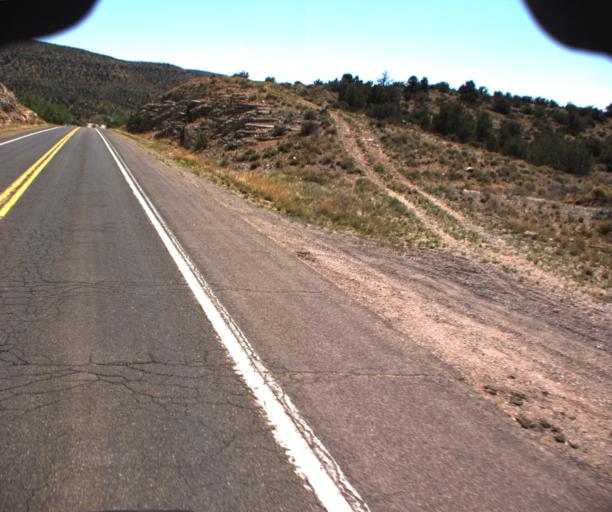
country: US
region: Arizona
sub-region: Mohave County
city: Peach Springs
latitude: 35.5343
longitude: -113.4202
